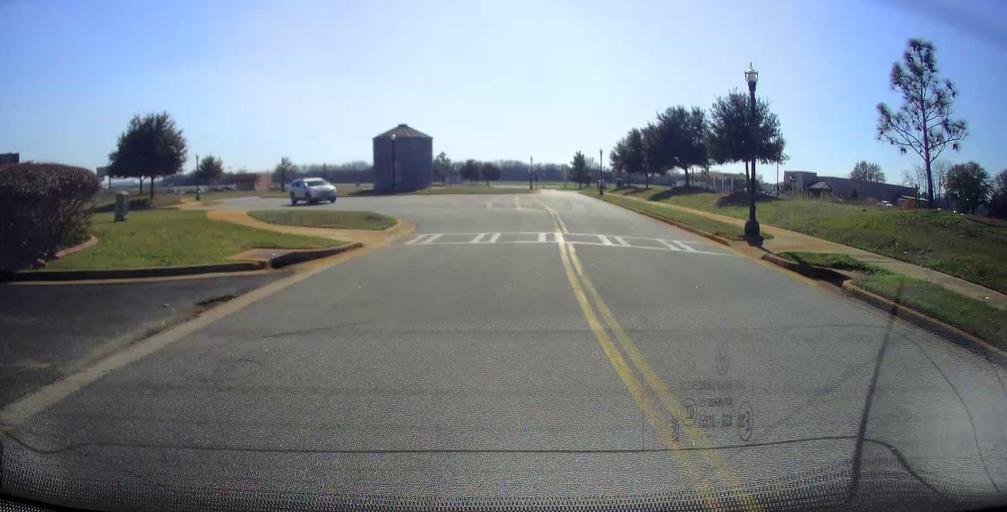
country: US
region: Georgia
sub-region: Houston County
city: Perry
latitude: 32.4348
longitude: -83.7592
